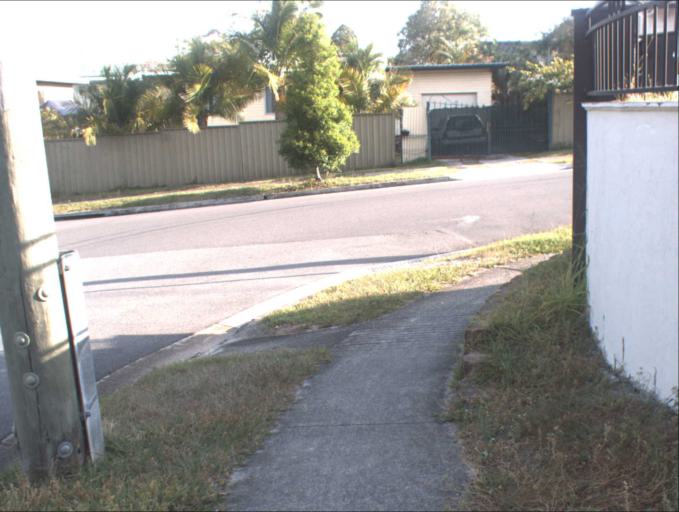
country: AU
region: Queensland
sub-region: Logan
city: Logan City
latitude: -27.6288
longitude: 153.1143
